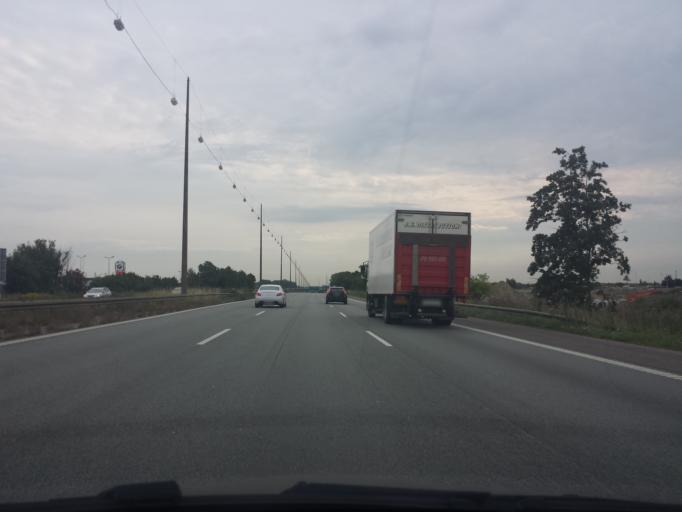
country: DK
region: Capital Region
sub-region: Vallensbaek Kommune
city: Vallensbaek
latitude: 55.6423
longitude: 12.3874
